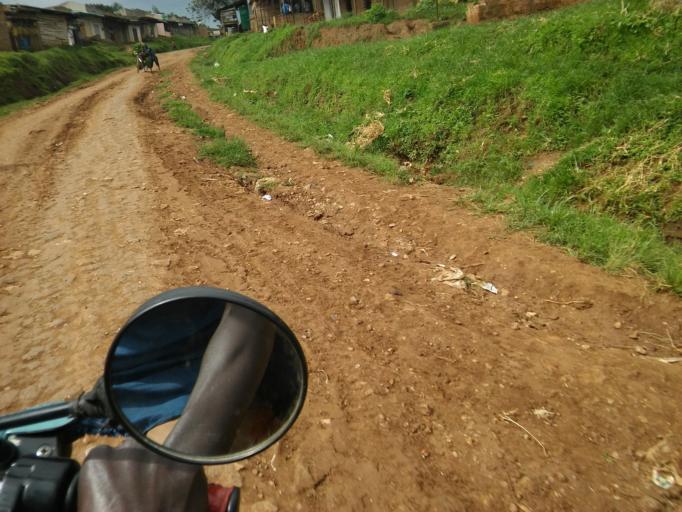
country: UG
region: Eastern Region
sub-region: Manafwa District
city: Manafwa
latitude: 0.9053
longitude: 34.3566
